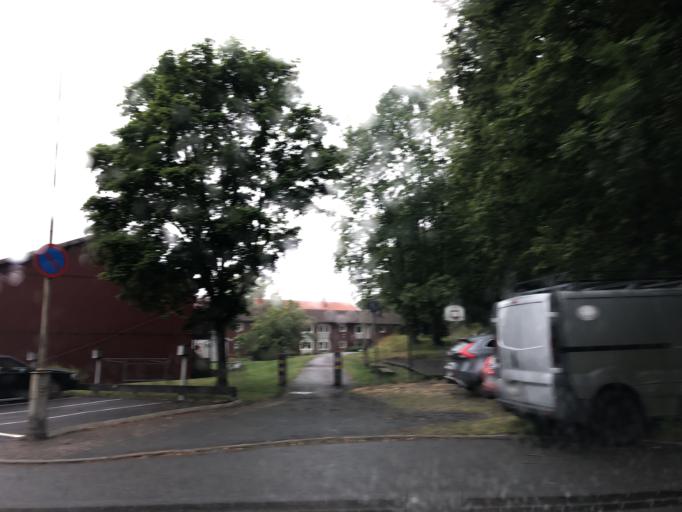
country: SE
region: Vaestra Goetaland
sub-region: Goteborg
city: Goeteborg
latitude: 57.7325
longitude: 11.9342
